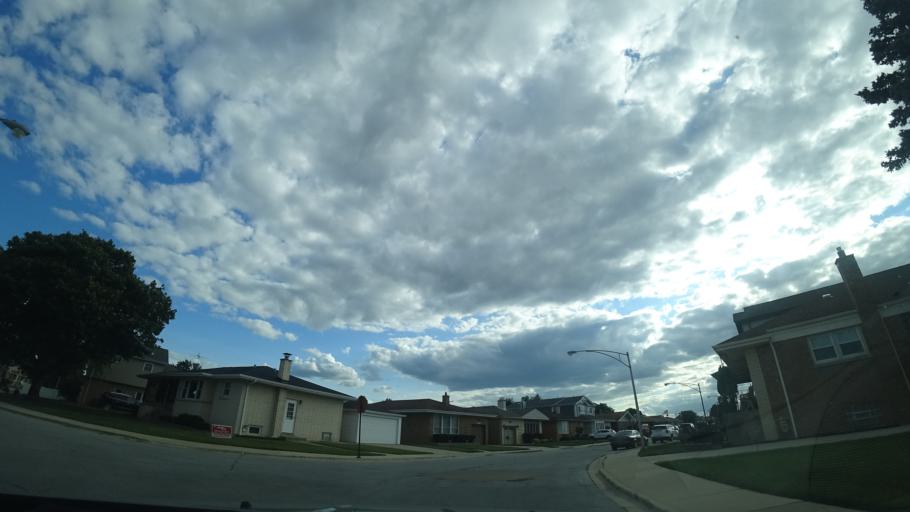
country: US
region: Illinois
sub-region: Cook County
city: Merrionette Park
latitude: 41.6879
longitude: -87.7117
